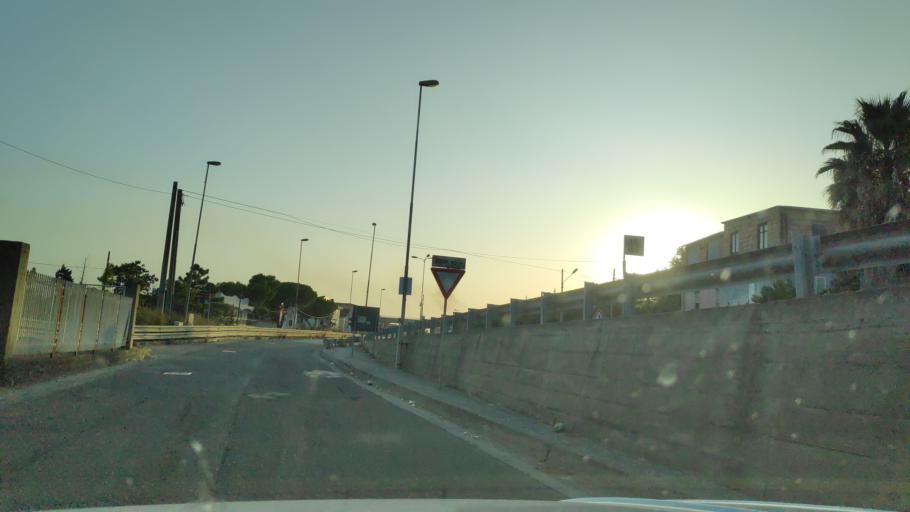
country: IT
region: Calabria
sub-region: Provincia di Reggio Calabria
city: Bova Marina
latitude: 37.9286
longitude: 15.9044
